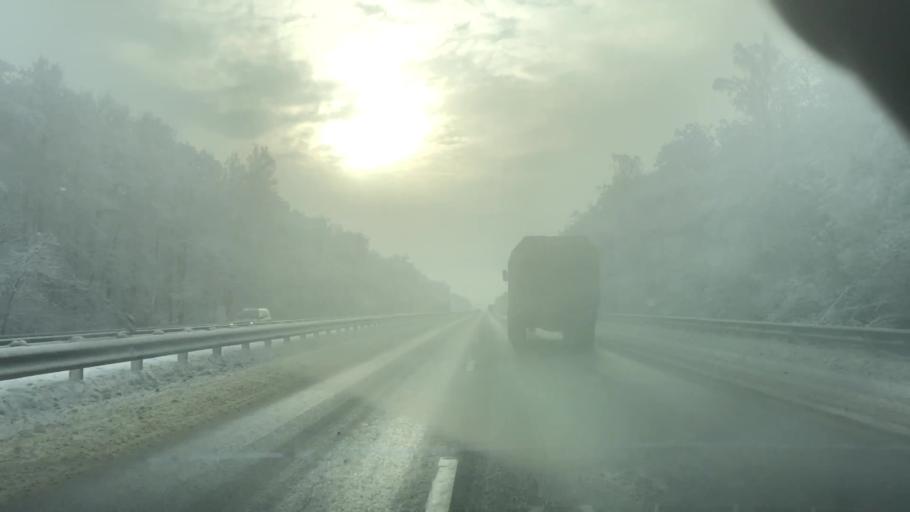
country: RU
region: Tula
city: Venev
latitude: 54.3691
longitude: 38.1547
